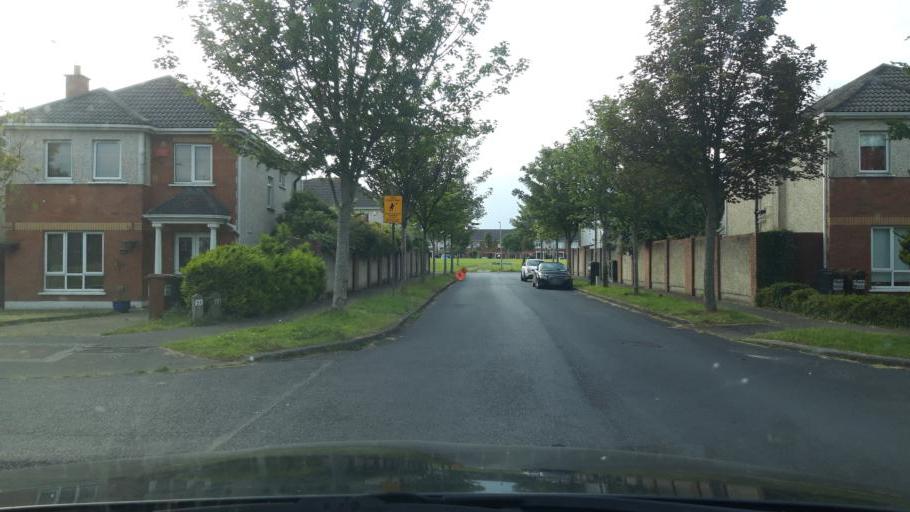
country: IE
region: Leinster
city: Hartstown
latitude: 53.4009
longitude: -6.4305
